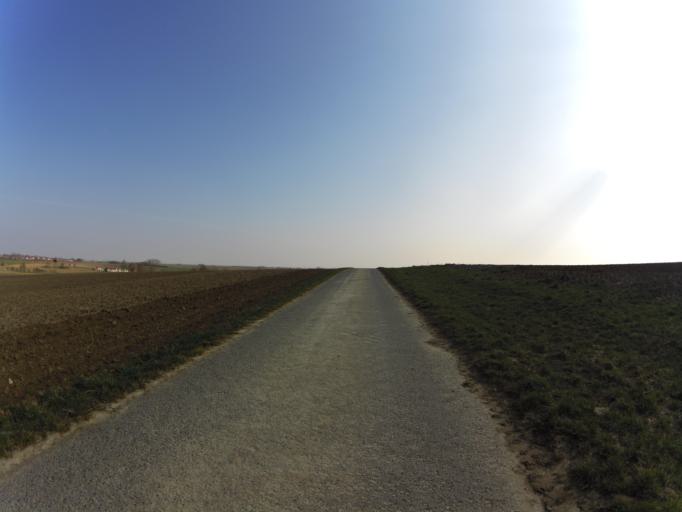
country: DE
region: Bavaria
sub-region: Regierungsbezirk Unterfranken
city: Sulzdorf
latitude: 49.6563
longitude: 9.9106
